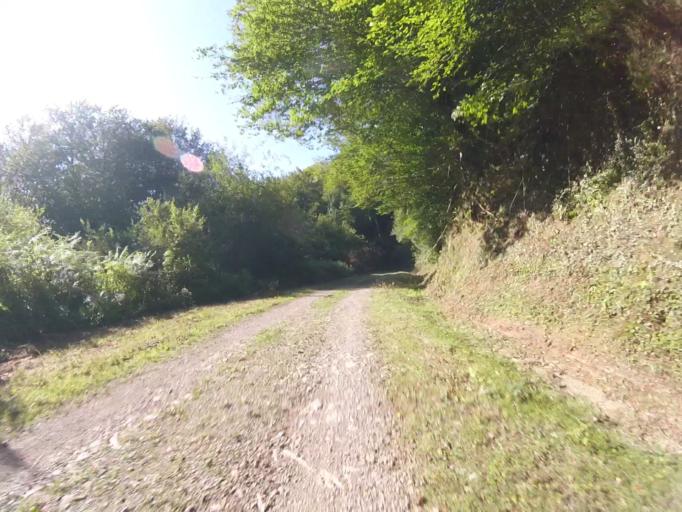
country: ES
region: Navarre
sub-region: Provincia de Navarra
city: Arano
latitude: 43.2450
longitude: -1.8902
